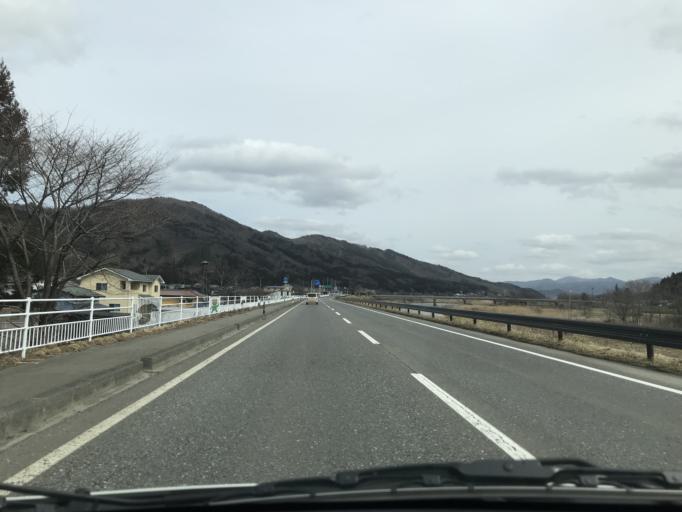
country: JP
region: Iwate
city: Tono
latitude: 39.3255
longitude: 141.4768
